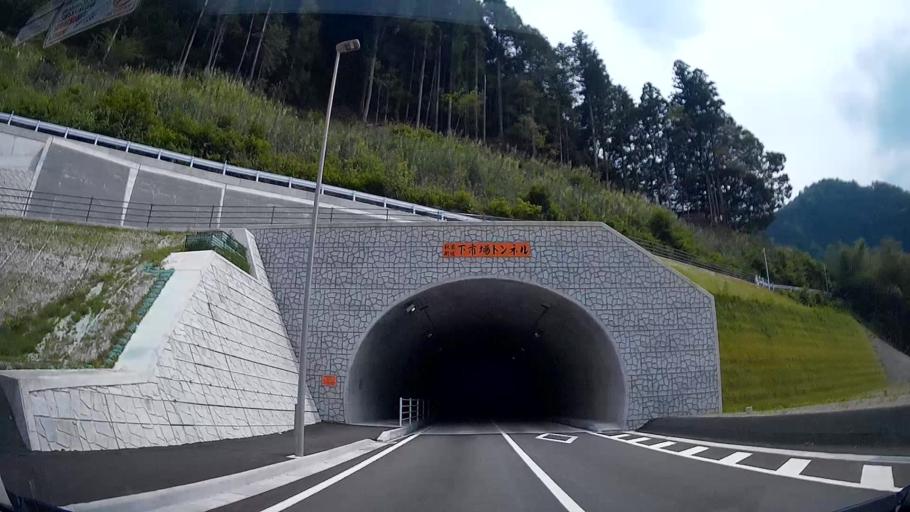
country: JP
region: Nagano
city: Iida
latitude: 35.3159
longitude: 137.9268
